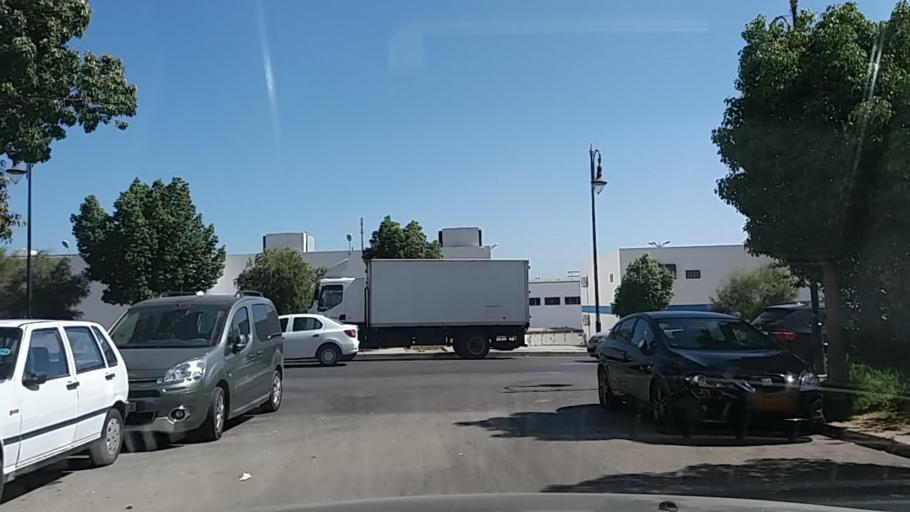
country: MA
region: Tanger-Tetouan
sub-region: Tanger-Assilah
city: Tangier
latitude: 35.7448
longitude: -5.8465
